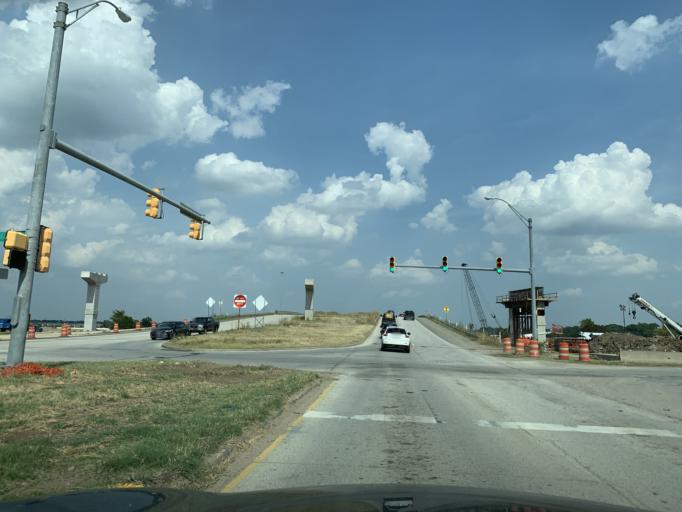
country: US
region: Texas
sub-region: Tarrant County
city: Richland Hills
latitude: 32.7977
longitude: -97.2140
